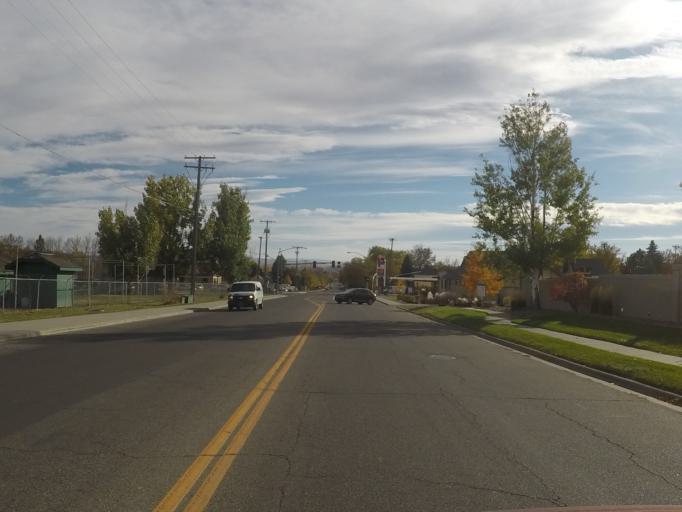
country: US
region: Montana
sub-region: Yellowstone County
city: Billings
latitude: 45.7961
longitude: -108.5592
